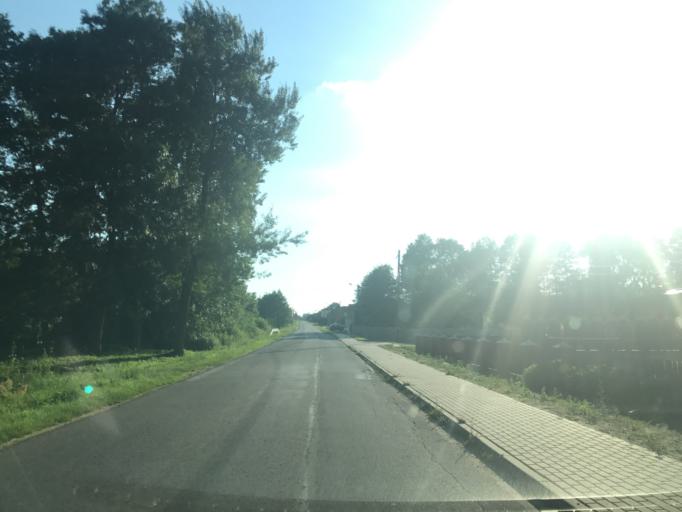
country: PL
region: Greater Poland Voivodeship
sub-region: Powiat turecki
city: Tuliszkow
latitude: 52.0945
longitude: 18.3708
